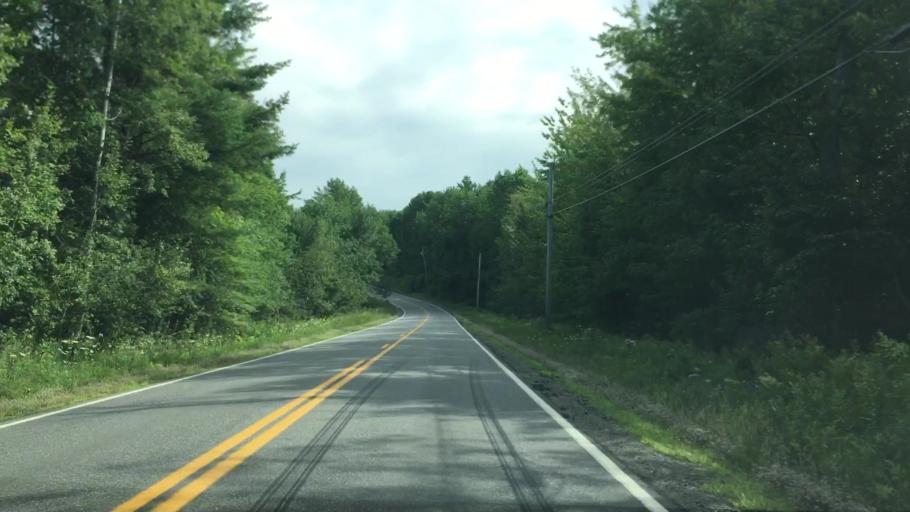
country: US
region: Maine
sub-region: Waldo County
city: Belfast
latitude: 44.3835
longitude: -69.0346
